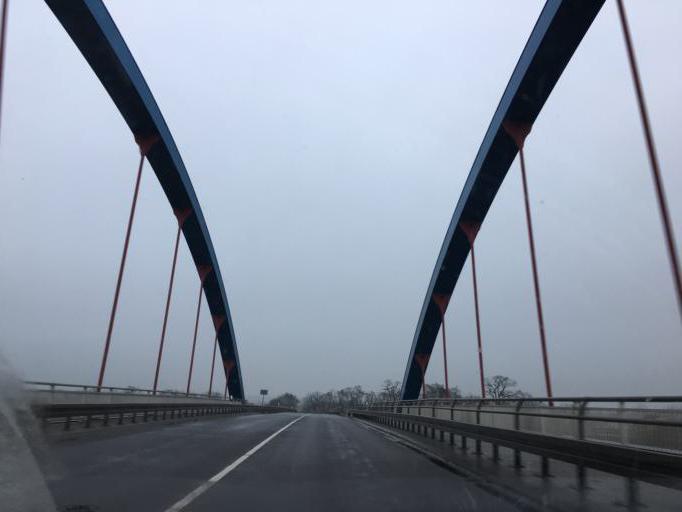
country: DE
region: Saxony-Anhalt
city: Gross Ammensleben
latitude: 52.2516
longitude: 11.4984
